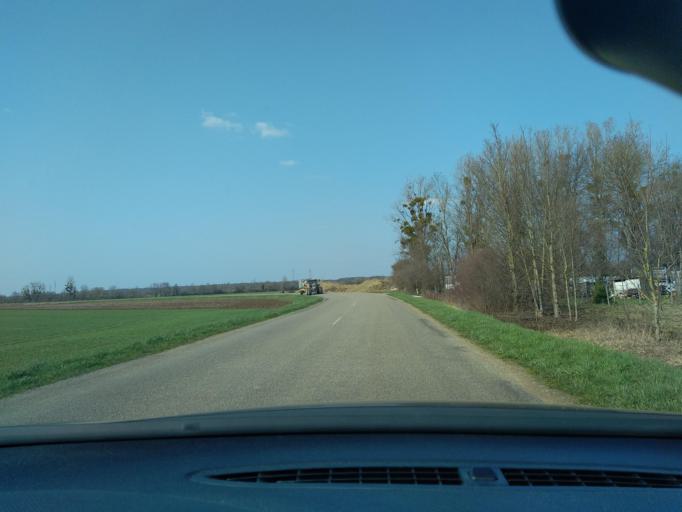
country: FR
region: Franche-Comte
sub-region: Departement du Jura
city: Mont-sous-Vaudrey
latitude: 46.9955
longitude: 5.6057
